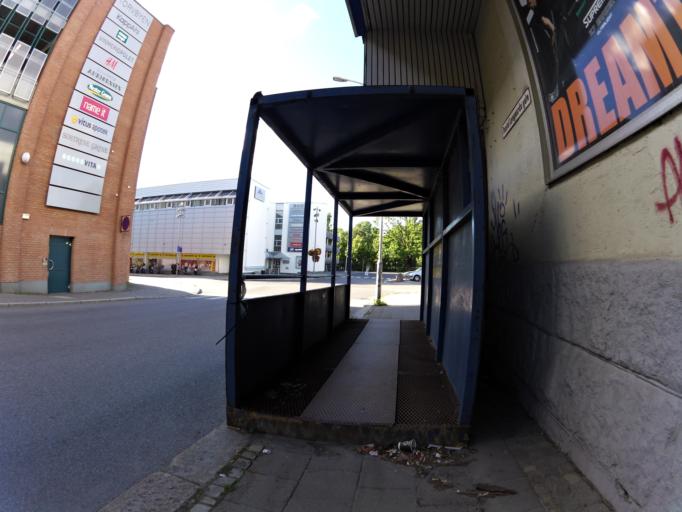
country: NO
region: Ostfold
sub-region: Fredrikstad
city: Fredrikstad
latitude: 59.2142
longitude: 10.9410
